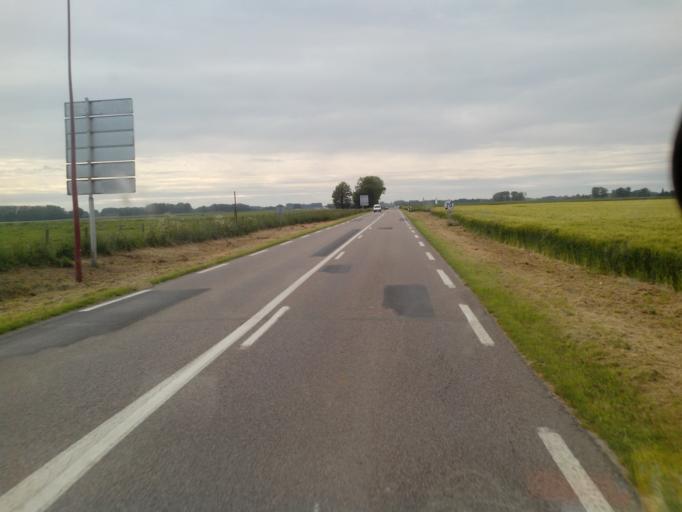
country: FR
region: Haute-Normandie
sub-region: Departement de la Seine-Maritime
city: Fauville-en-Caux
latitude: 49.6611
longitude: 0.5894
